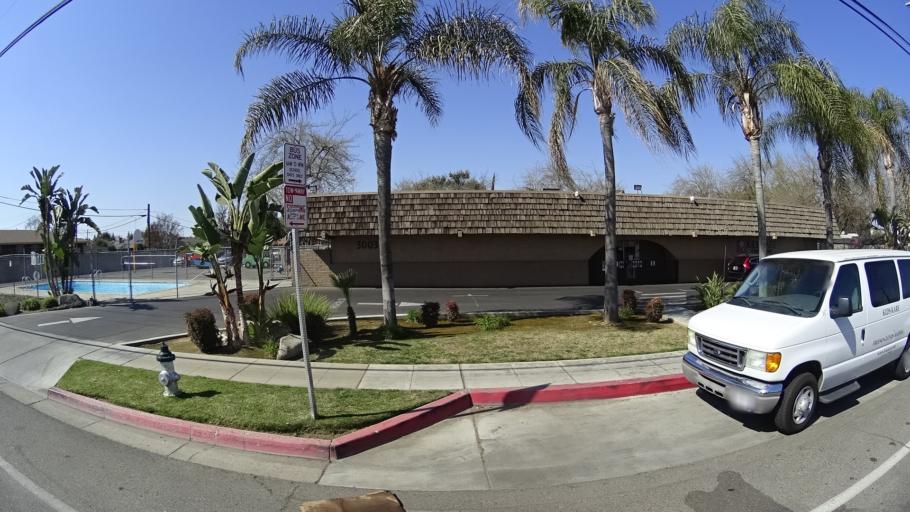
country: US
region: California
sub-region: Fresno County
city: Fresno
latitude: 36.7775
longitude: -119.8267
